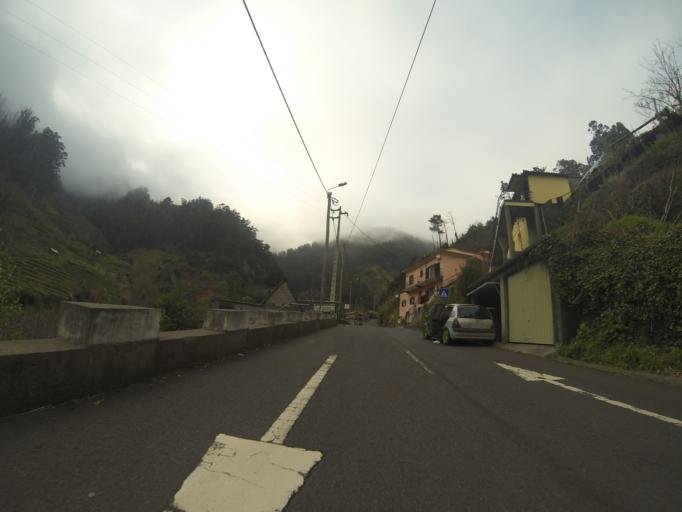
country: PT
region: Madeira
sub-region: Camara de Lobos
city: Curral das Freiras
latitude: 32.7431
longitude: -16.9654
